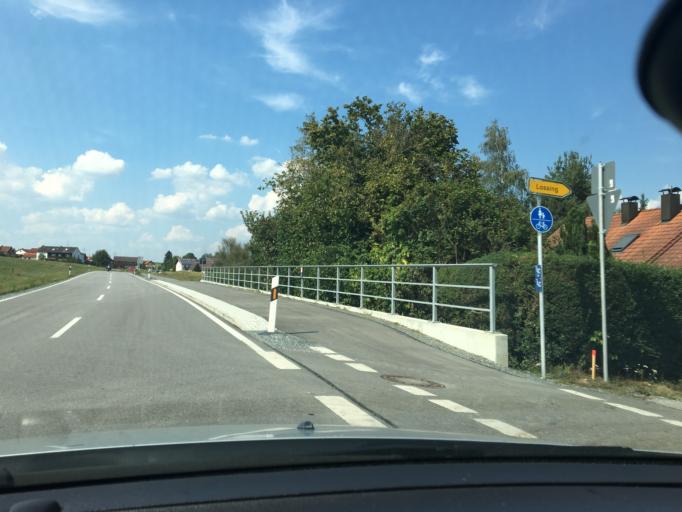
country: DE
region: Bavaria
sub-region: Upper Bavaria
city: Rohrbach
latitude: 48.3120
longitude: 12.5601
